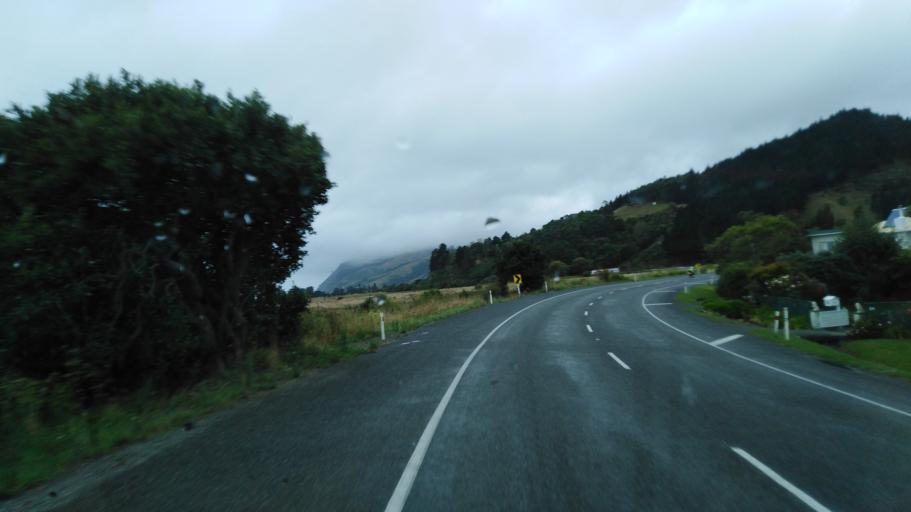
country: NZ
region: Nelson
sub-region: Nelson City
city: Nelson
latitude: -41.2145
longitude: 173.3308
